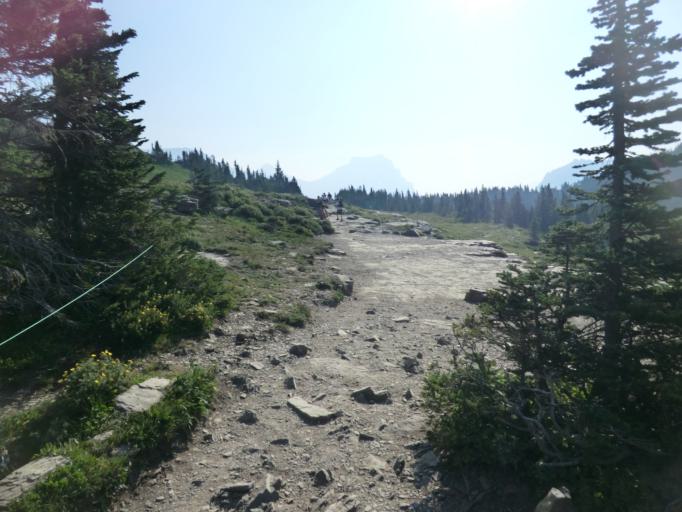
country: US
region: Montana
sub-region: Flathead County
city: Columbia Falls
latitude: 48.6873
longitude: -113.7413
